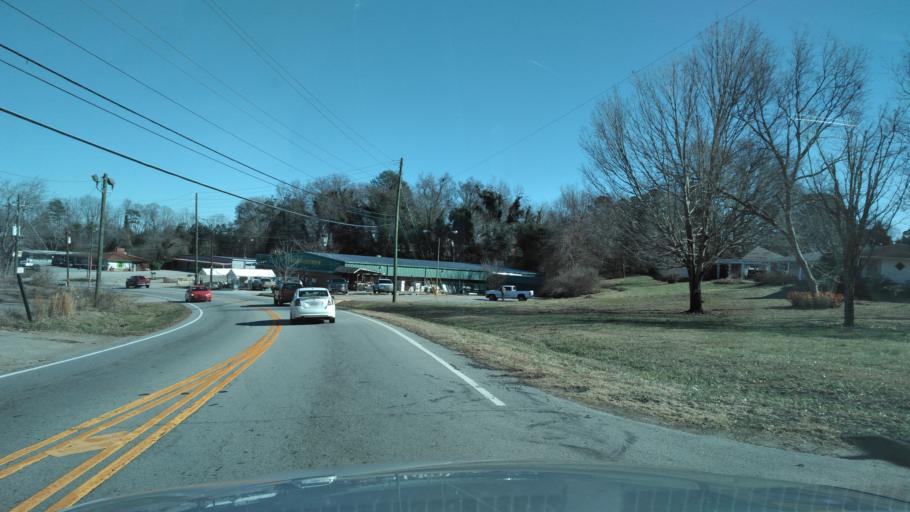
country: US
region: Georgia
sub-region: Hall County
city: Gainesville
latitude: 34.3122
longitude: -83.7732
